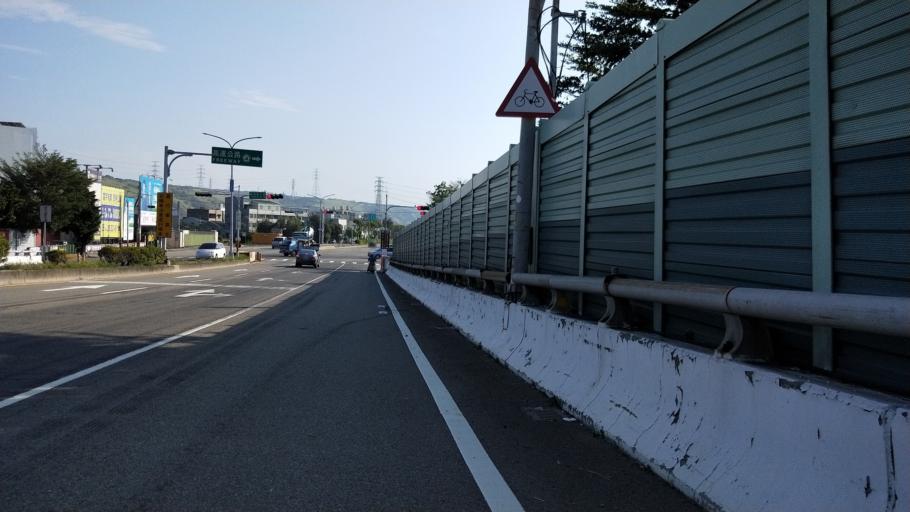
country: TW
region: Taiwan
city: Fengyuan
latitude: 24.3048
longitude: 120.5965
